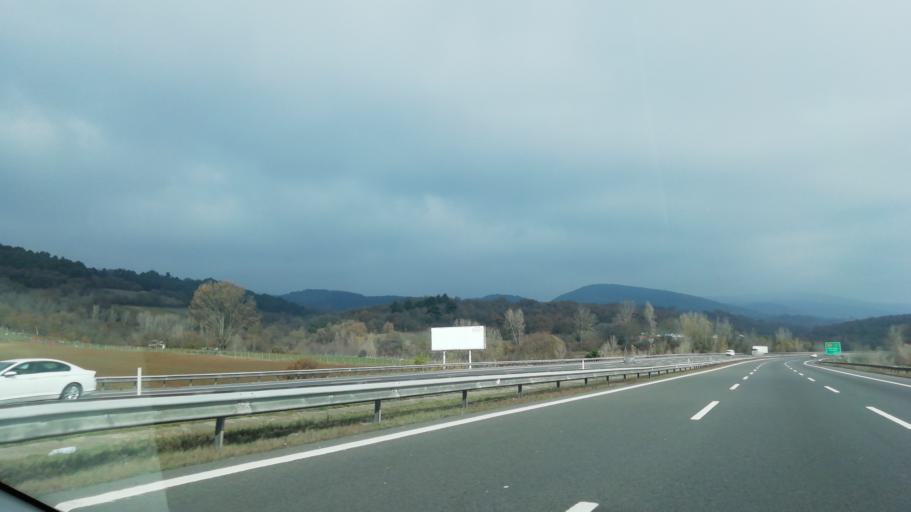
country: TR
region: Bolu
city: Bolu
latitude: 40.7371
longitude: 31.5355
